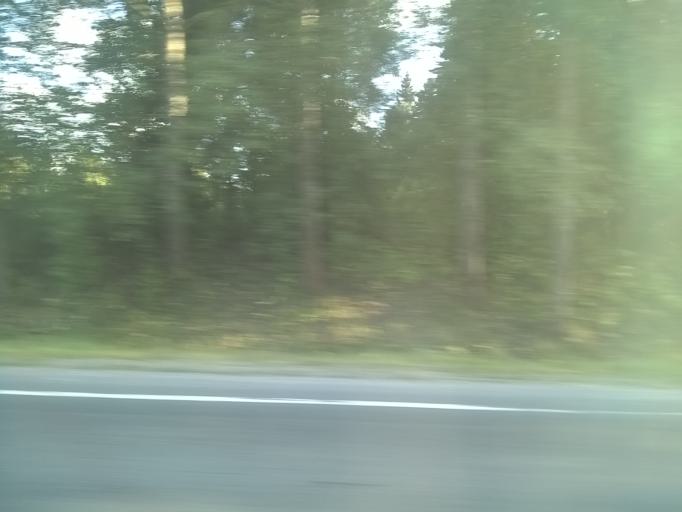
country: FI
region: Pirkanmaa
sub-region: Tampere
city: Tampere
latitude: 61.5059
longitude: 23.8372
